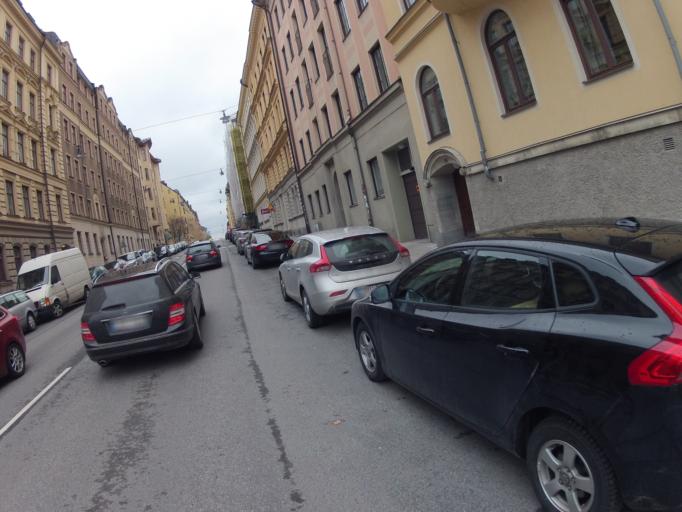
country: SE
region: Stockholm
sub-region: Stockholms Kommun
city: Stockholm
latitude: 59.3431
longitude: 18.0443
